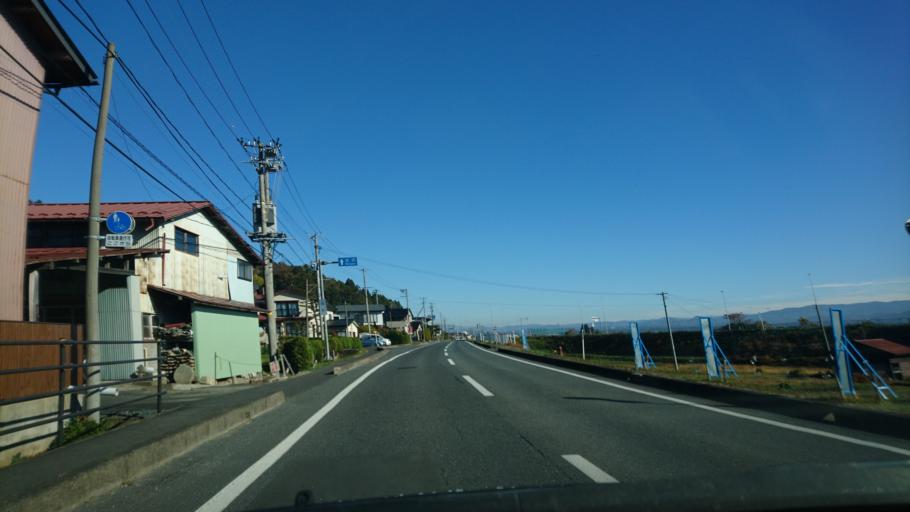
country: JP
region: Iwate
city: Mizusawa
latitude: 39.0718
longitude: 141.1299
